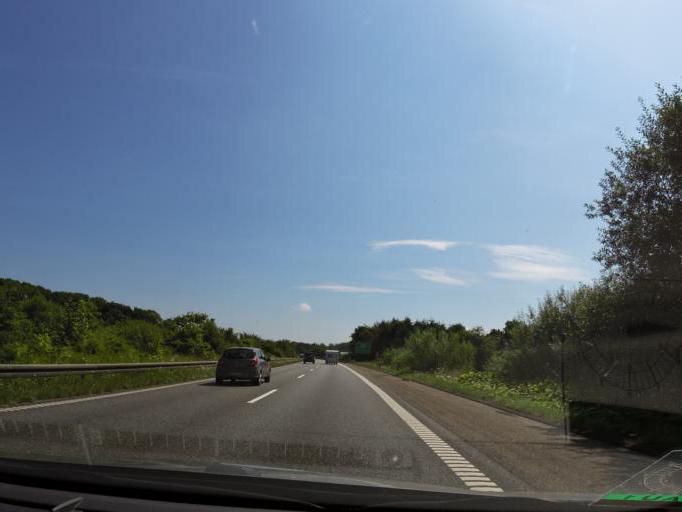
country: DK
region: South Denmark
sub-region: Fredericia Kommune
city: Taulov
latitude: 55.5408
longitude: 9.6565
